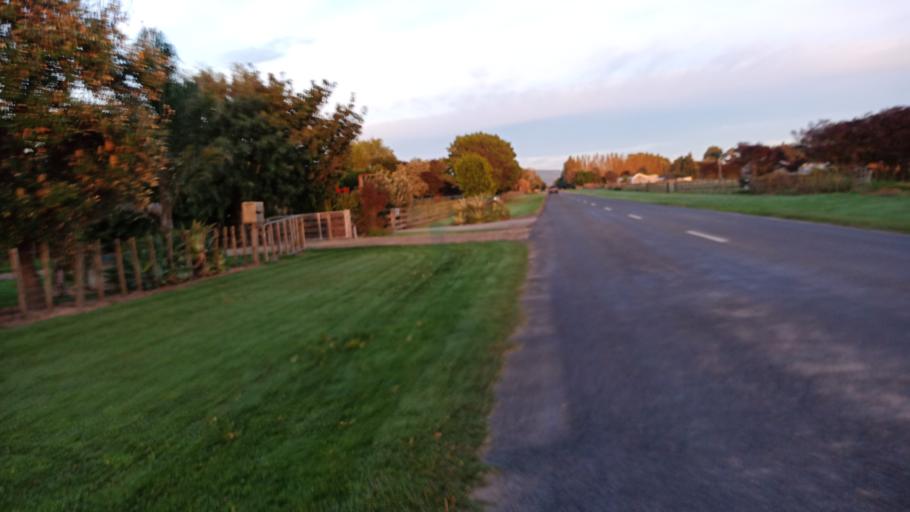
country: NZ
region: Gisborne
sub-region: Gisborne District
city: Gisborne
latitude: -38.6336
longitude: 177.9851
